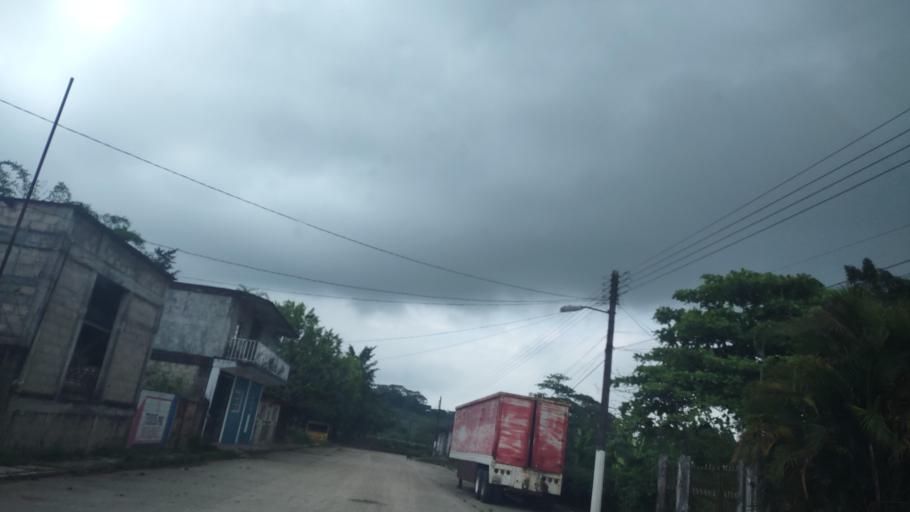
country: MX
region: Veracruz
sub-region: Uxpanapa
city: Poblado 10
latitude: 17.4950
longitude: -94.1624
